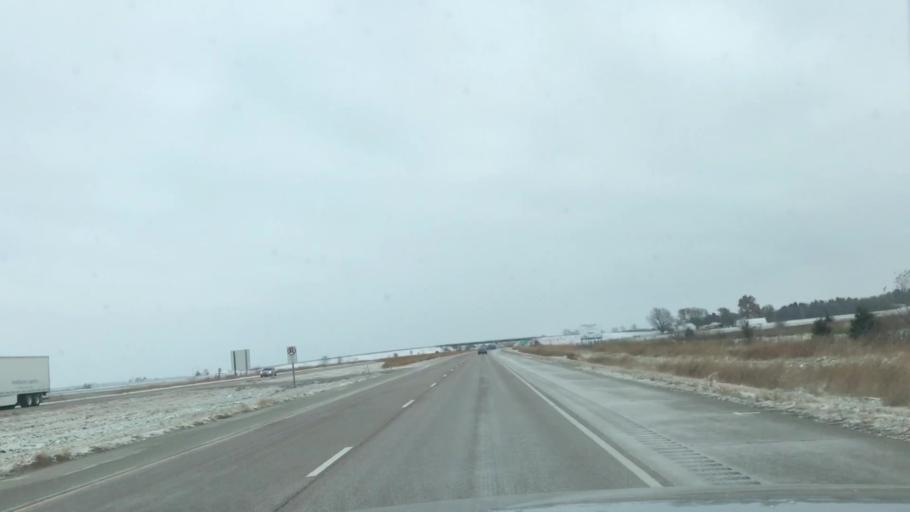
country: US
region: Illinois
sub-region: Montgomery County
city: Litchfield
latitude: 39.1839
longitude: -89.6751
